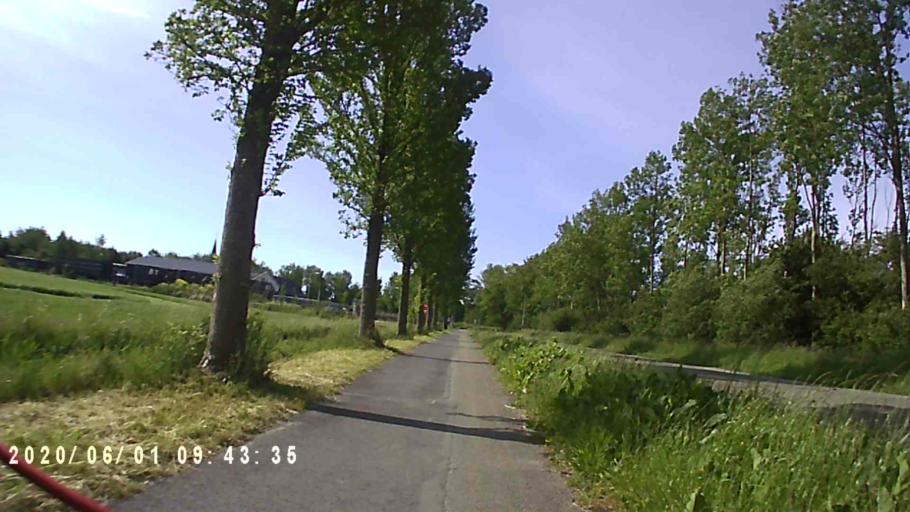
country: NL
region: Friesland
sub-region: Menameradiel
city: Menaam
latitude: 53.2403
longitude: 5.6838
